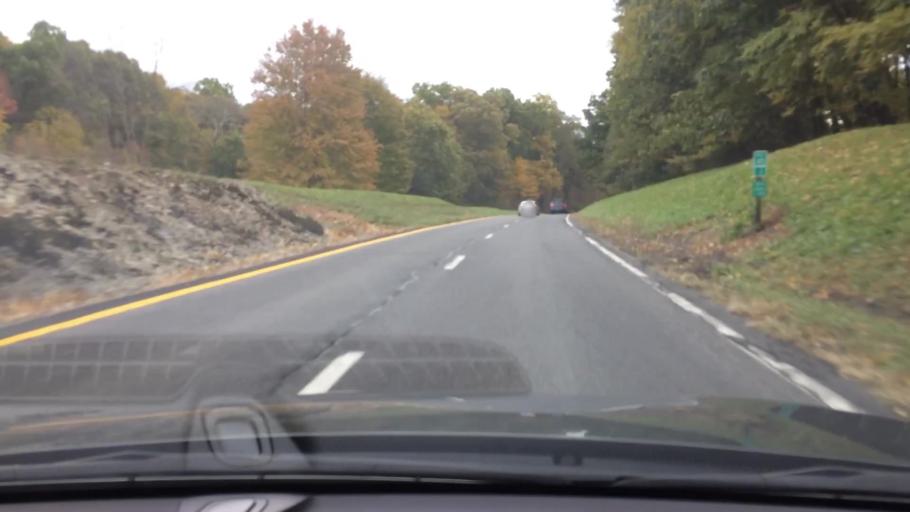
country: US
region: New York
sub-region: Dutchess County
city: Hillside Lake
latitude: 41.6392
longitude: -73.7851
